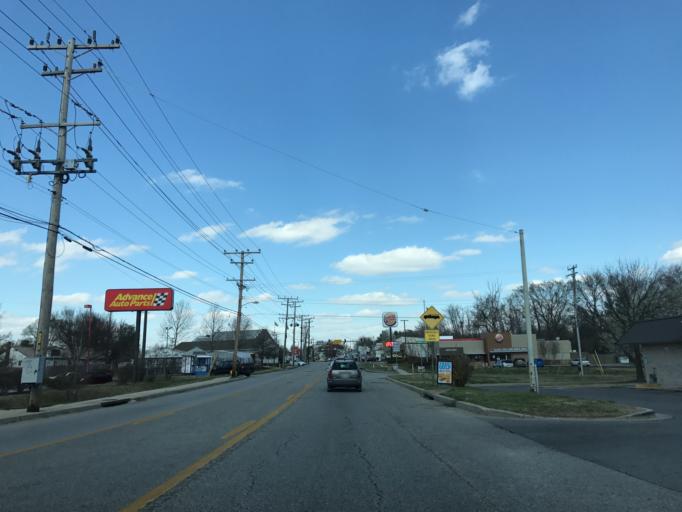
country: US
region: Maryland
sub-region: Anne Arundel County
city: Riviera Beach
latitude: 39.1548
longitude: -76.5179
